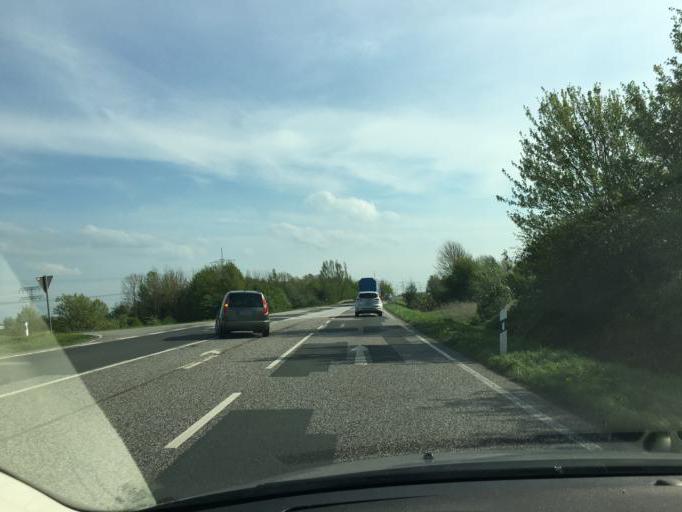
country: DE
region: Saxony-Anhalt
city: Meitzendorf
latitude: 52.2117
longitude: 11.5469
